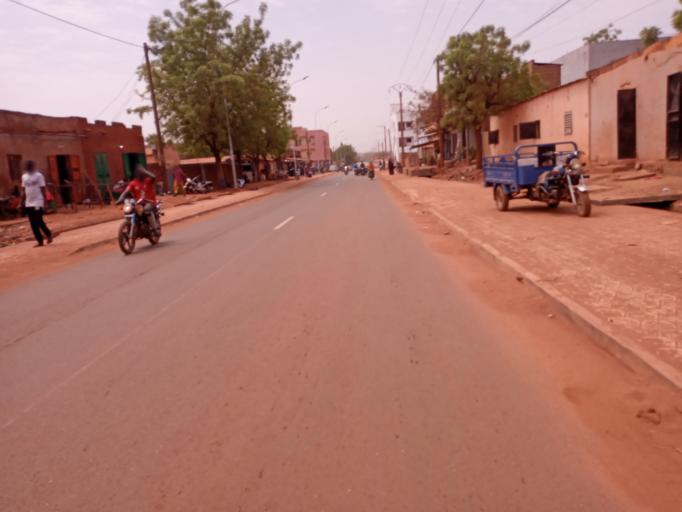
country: ML
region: Bamako
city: Bamako
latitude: 12.5873
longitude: -7.9882
